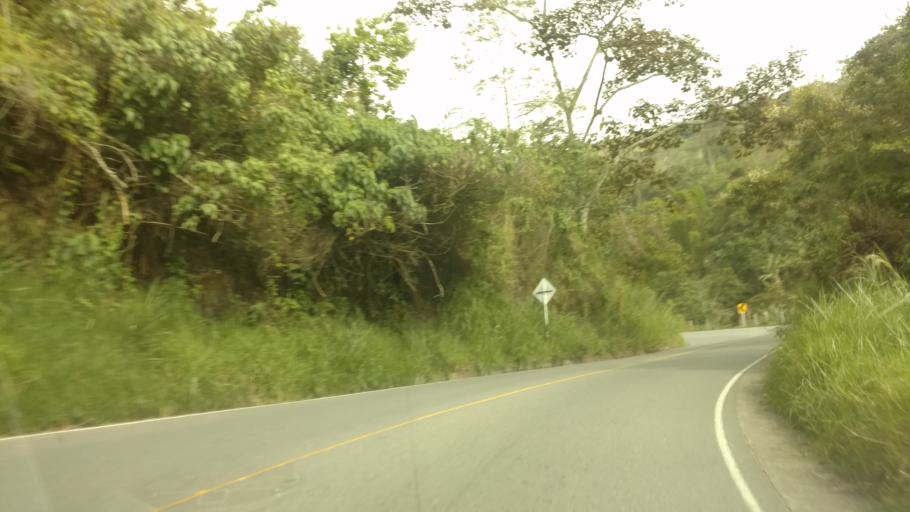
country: CO
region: Caldas
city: Neira
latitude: 5.1392
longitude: -75.4951
